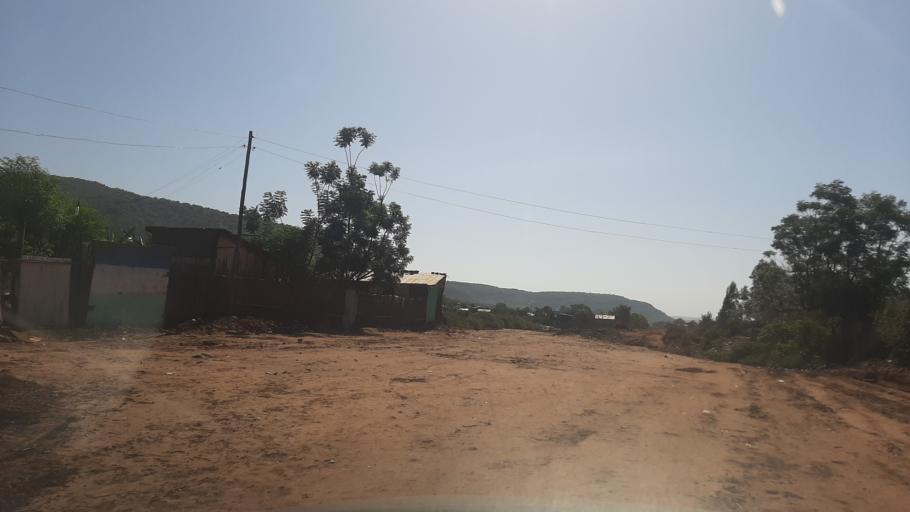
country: ET
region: Oromiya
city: Yabelo
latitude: 4.8942
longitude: 38.0995
